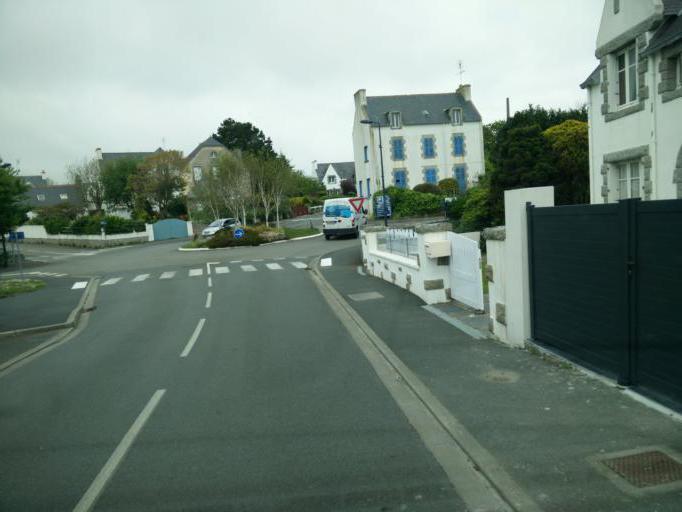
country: FR
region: Brittany
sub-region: Departement du Finistere
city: Plobannalec-Lesconil
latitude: 47.8012
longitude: -4.2178
